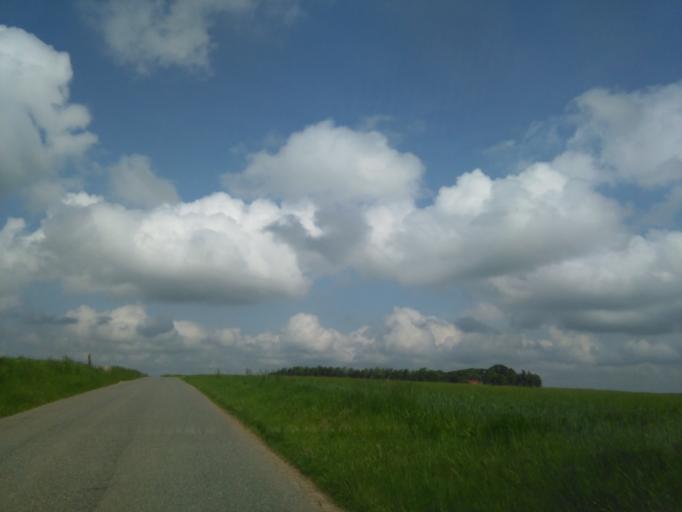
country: DK
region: Central Jutland
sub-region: Arhus Kommune
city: Sabro
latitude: 56.2013
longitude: 9.9960
